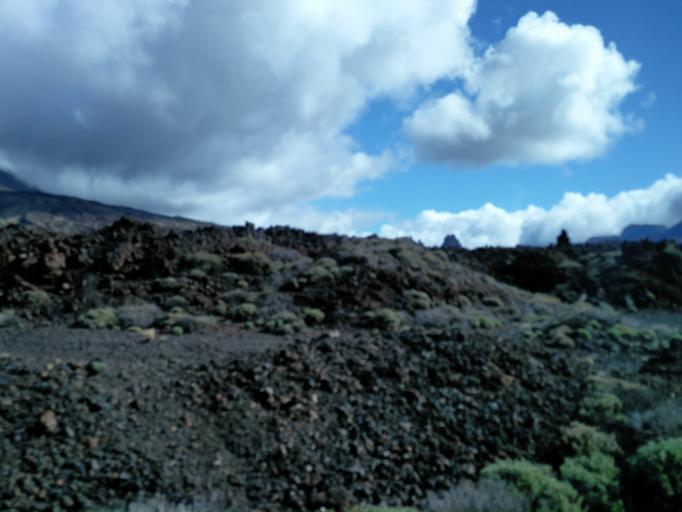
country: ES
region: Canary Islands
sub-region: Provincia de Santa Cruz de Tenerife
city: Vilaflor
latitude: 28.2151
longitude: -16.6675
